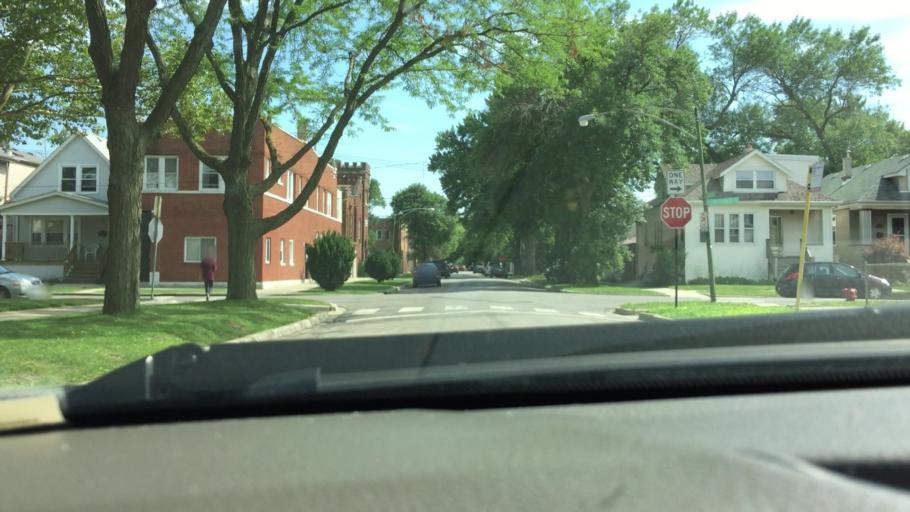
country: US
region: Illinois
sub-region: Cook County
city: Harwood Heights
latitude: 41.9509
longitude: -87.7522
